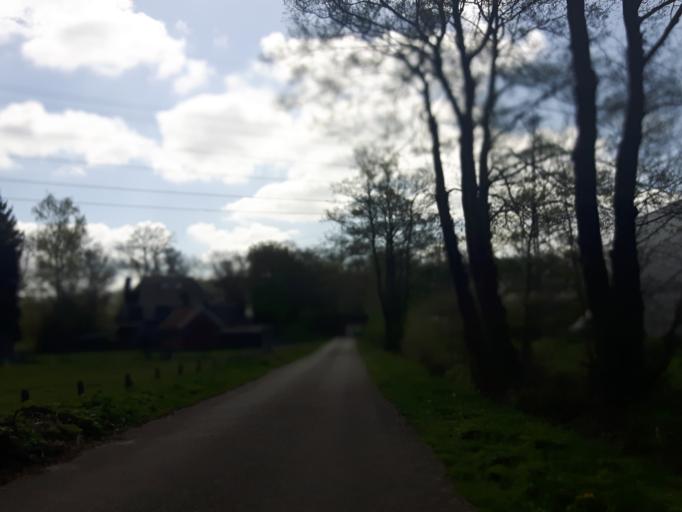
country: NL
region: Overijssel
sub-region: Gemeente Hengelo
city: Hengelo
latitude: 52.2158
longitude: 6.8312
